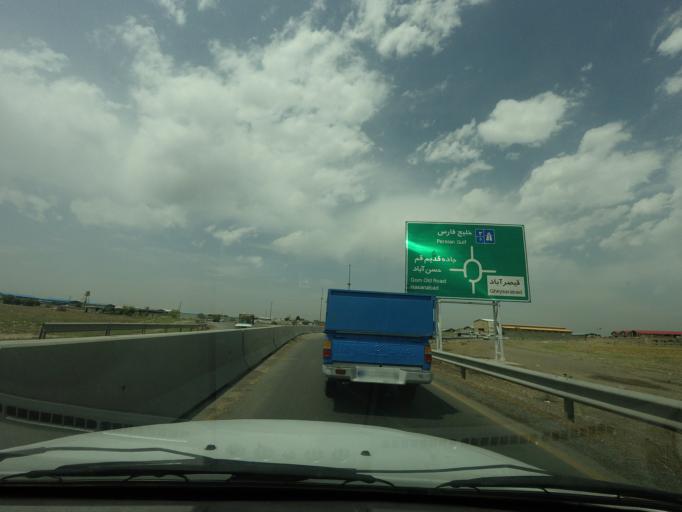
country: IR
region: Tehran
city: Shahrak-e Emam Hasan-e Mojtaba
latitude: 35.5066
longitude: 51.3234
